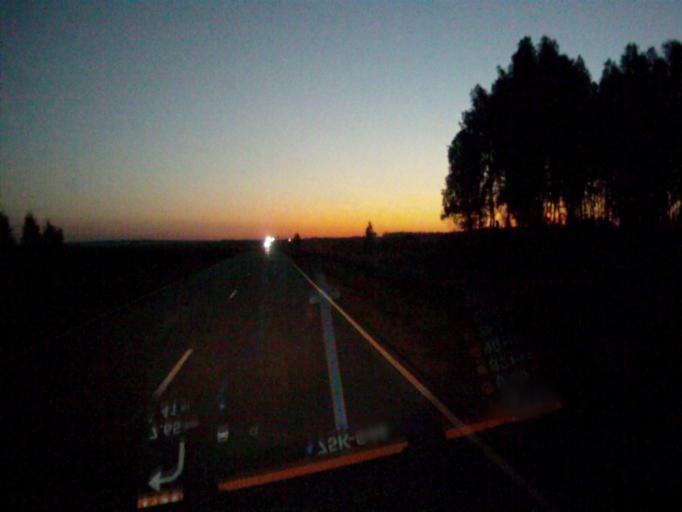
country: RU
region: Chelyabinsk
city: Chebarkul'
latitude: 55.2205
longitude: 60.5689
